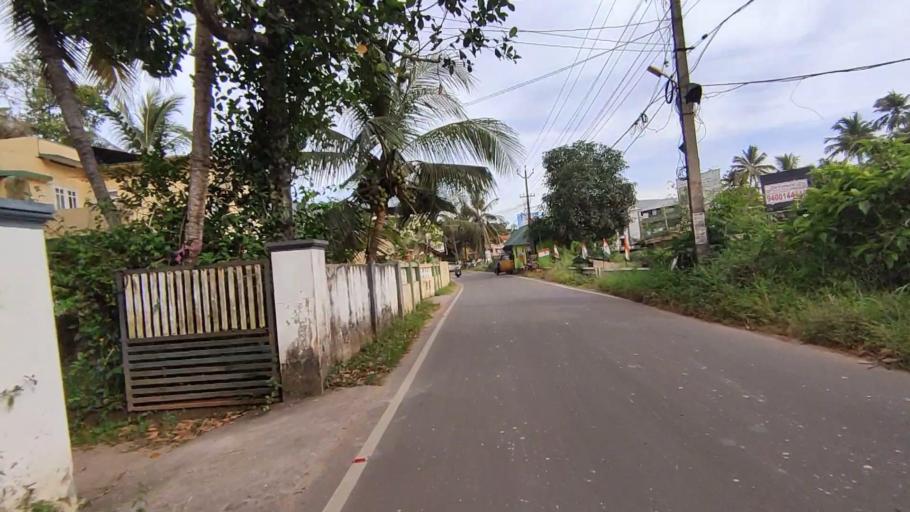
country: IN
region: Kerala
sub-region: Kottayam
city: Kottayam
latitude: 9.5913
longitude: 76.4972
